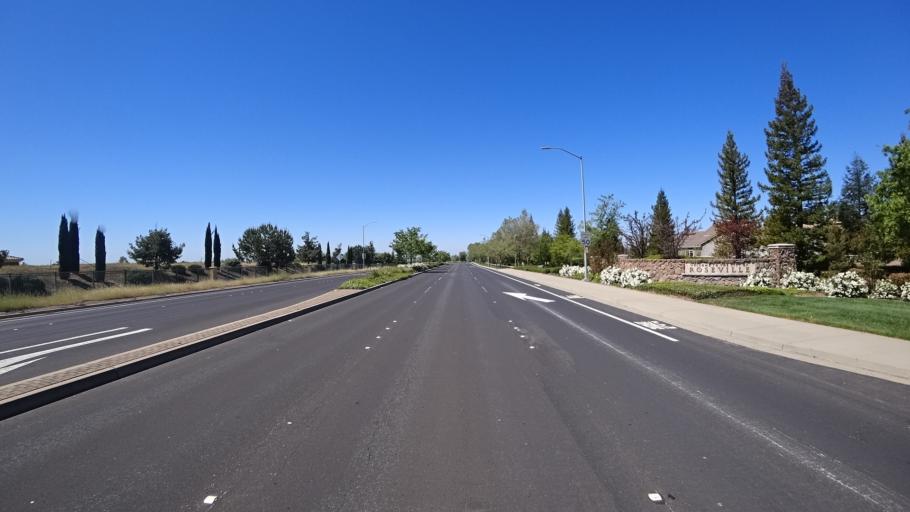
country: US
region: California
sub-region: Placer County
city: Rocklin
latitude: 38.7700
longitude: -121.2187
